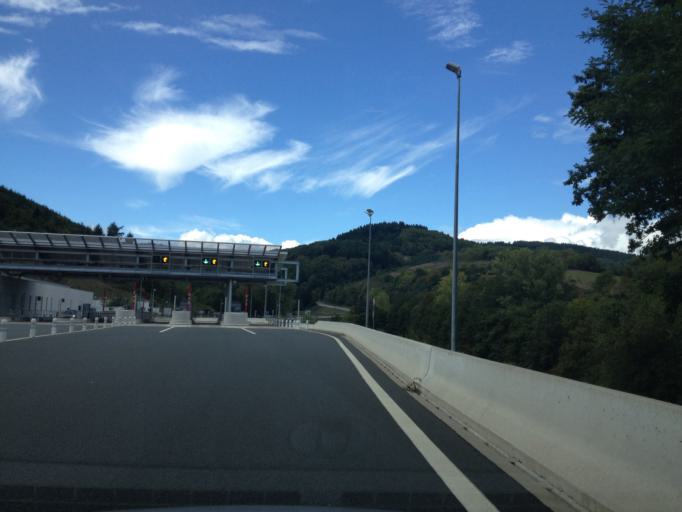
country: FR
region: Rhone-Alpes
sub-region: Departement du Rhone
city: Tarare
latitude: 45.8915
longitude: 4.4041
